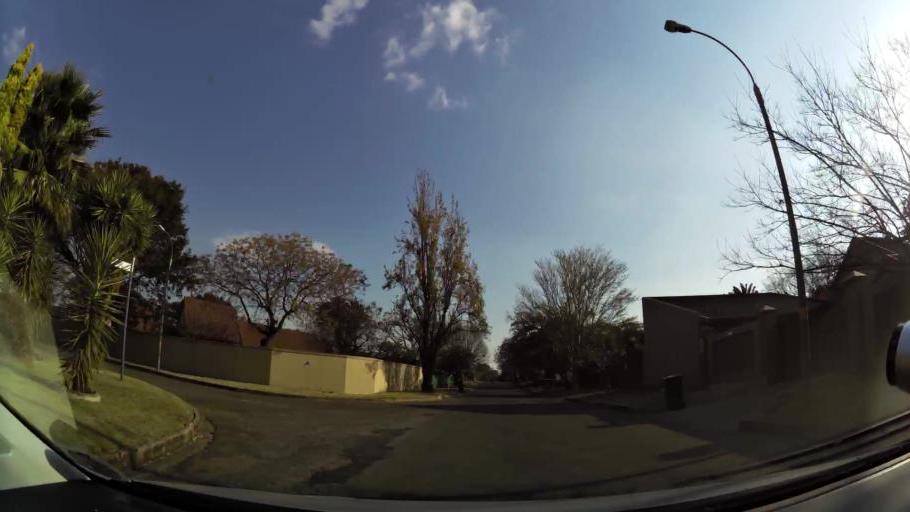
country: ZA
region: Gauteng
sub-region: City of Johannesburg Metropolitan Municipality
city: Modderfontein
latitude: -26.0761
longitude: 28.2075
